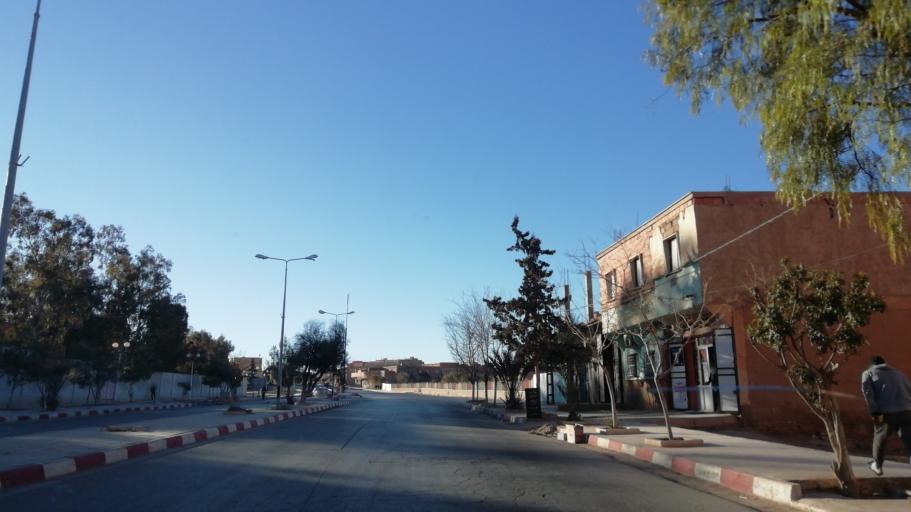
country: DZ
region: Saida
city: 'Ain el Hadjar
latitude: 34.0363
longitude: 0.0875
